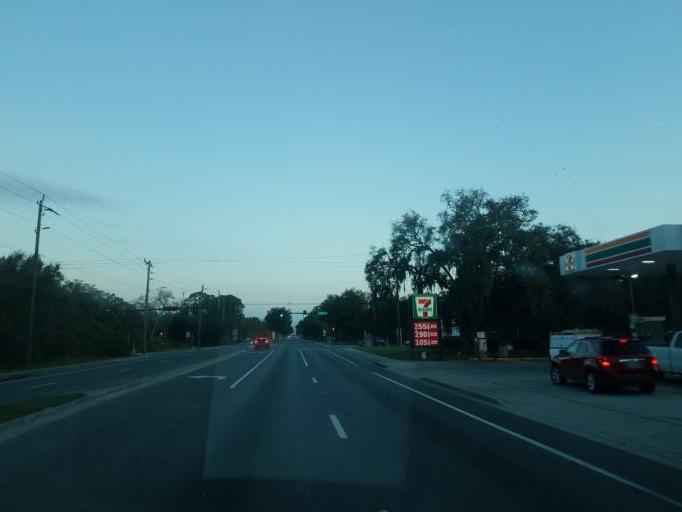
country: US
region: Florida
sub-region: Sarasota County
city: North Sarasota
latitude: 27.3809
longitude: -82.5056
